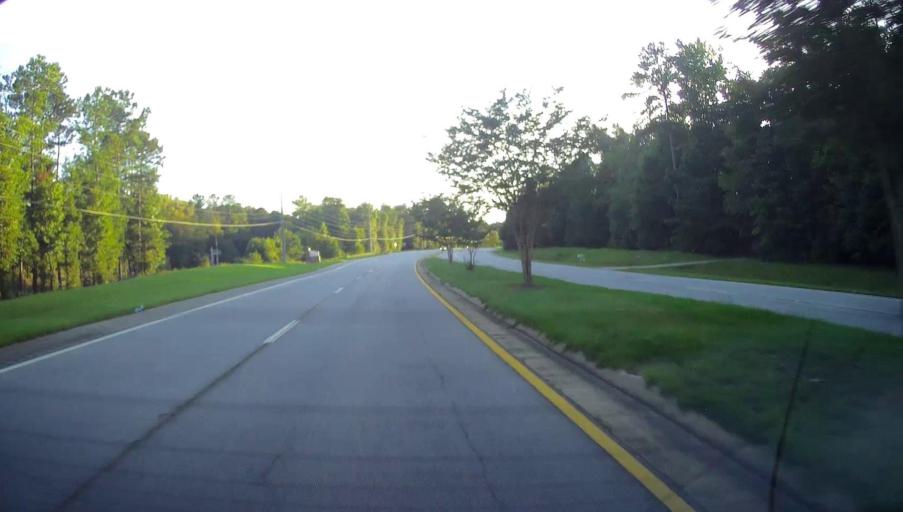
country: US
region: Georgia
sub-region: Muscogee County
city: Columbus
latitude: 32.5265
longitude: -84.8579
